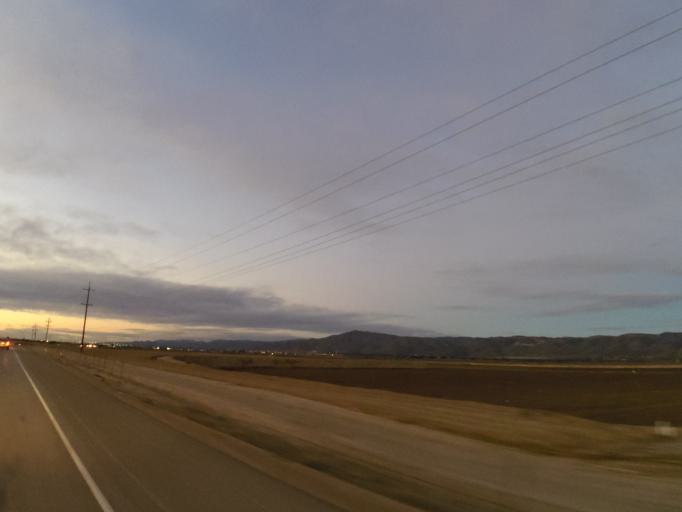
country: US
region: California
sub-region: Monterey County
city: Soledad
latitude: 36.3845
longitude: -121.3012
